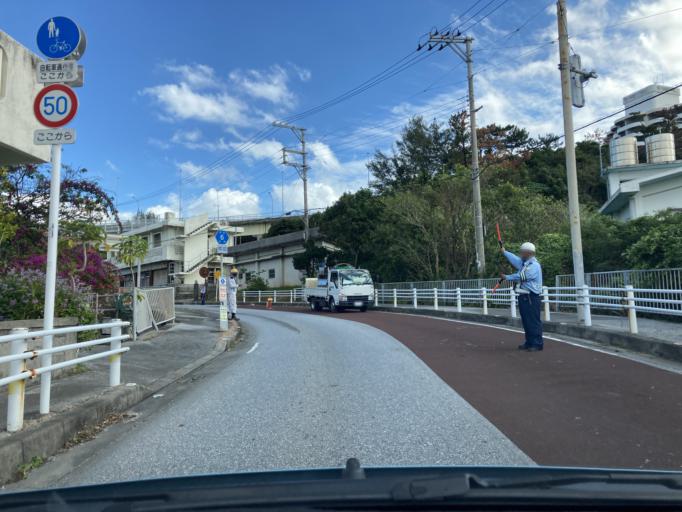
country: JP
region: Okinawa
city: Ishikawa
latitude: 26.4385
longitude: 127.8024
